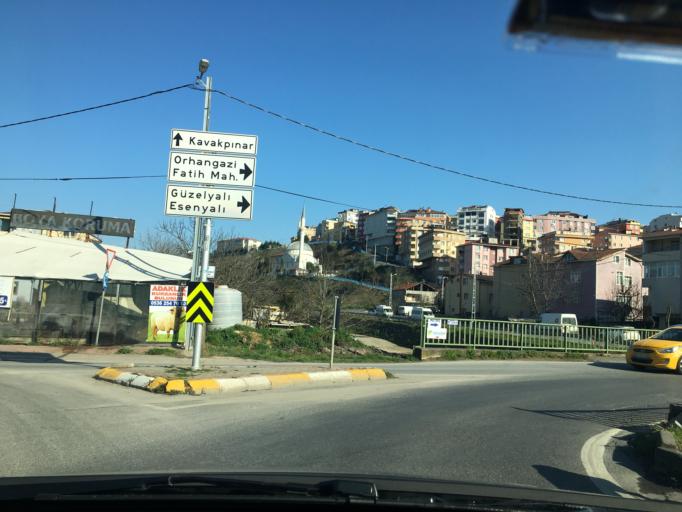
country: TR
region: Istanbul
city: Pendik
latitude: 40.8719
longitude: 29.2889
